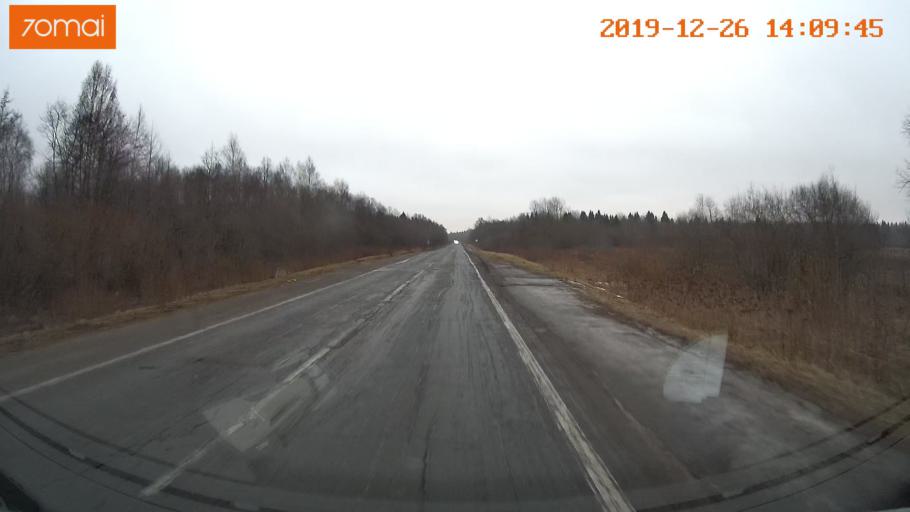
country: RU
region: Jaroslavl
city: Poshekhon'ye
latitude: 58.5085
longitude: 38.9396
